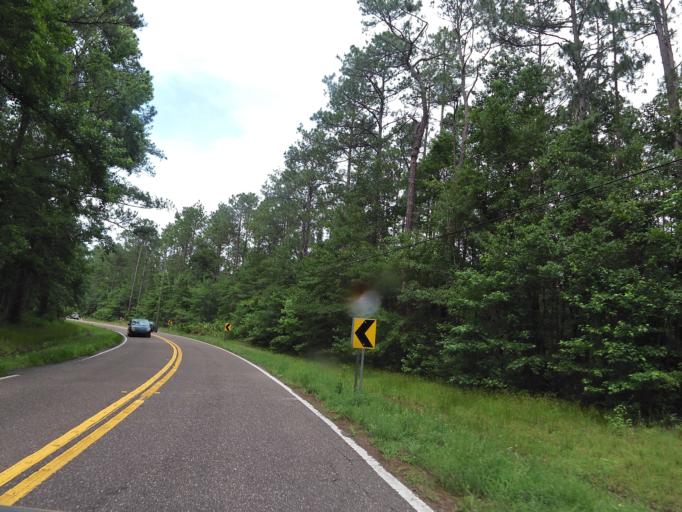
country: US
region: Florida
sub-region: Nassau County
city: Nassau Village-Ratliff
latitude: 30.5313
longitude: -81.7273
